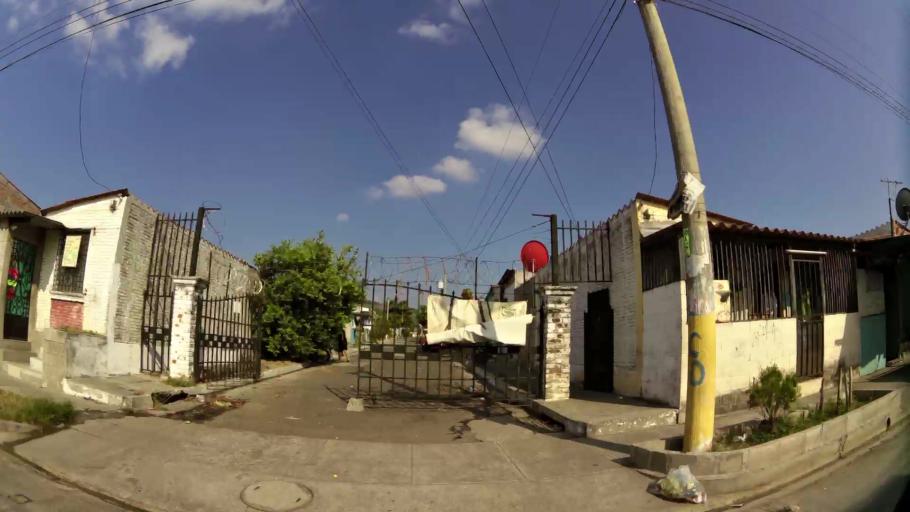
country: SV
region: San Salvador
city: Ilopango
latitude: 13.7272
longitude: -89.1114
